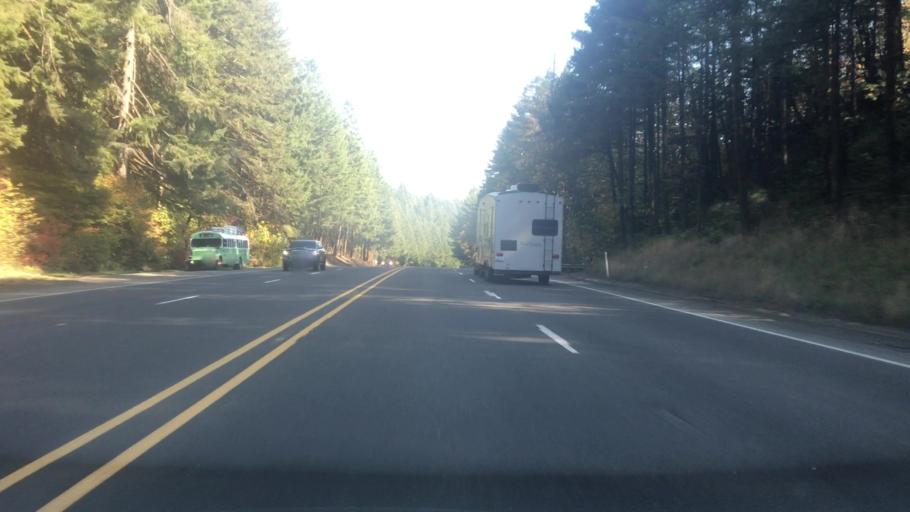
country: US
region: Oregon
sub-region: Polk County
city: Grand Ronde
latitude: 45.0607
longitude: -123.6964
